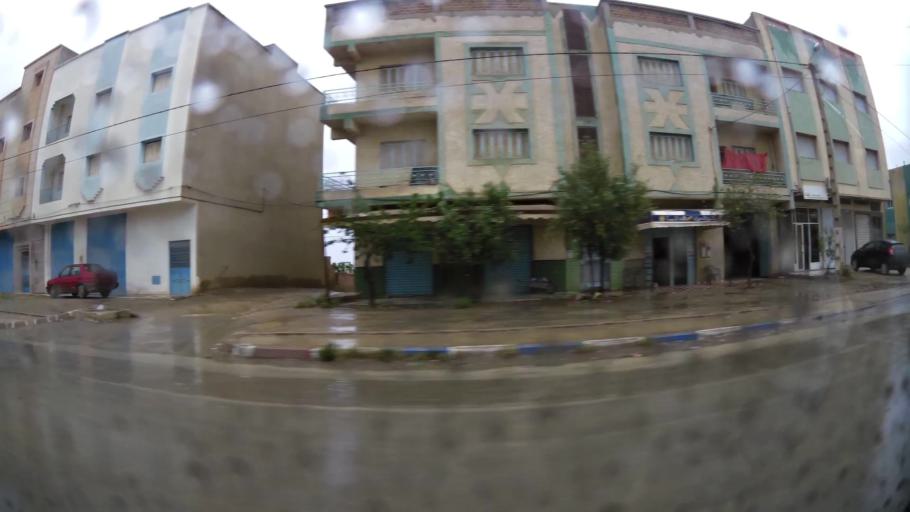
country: MA
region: Oriental
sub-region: Nador
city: Midar
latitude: 34.8857
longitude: -3.7272
